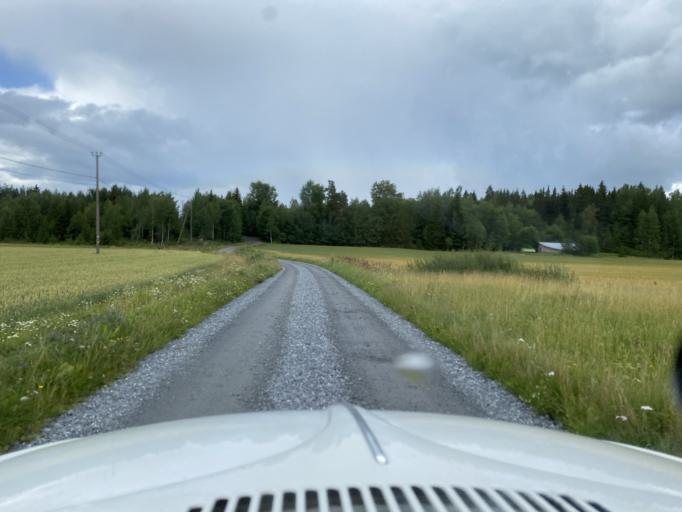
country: FI
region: Pirkanmaa
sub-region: Lounais-Pirkanmaa
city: Punkalaidun
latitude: 61.1257
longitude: 23.0630
